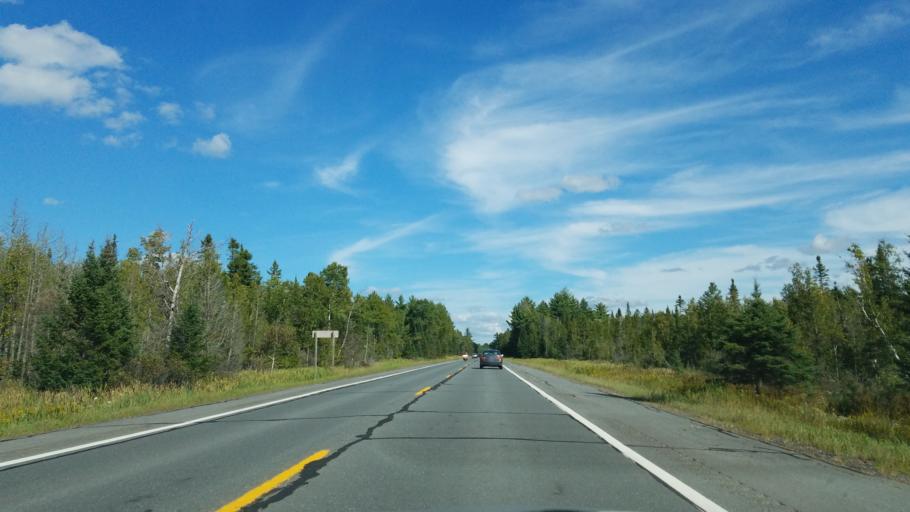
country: US
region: Michigan
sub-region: Baraga County
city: L'Anse
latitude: 46.5789
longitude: -88.3944
